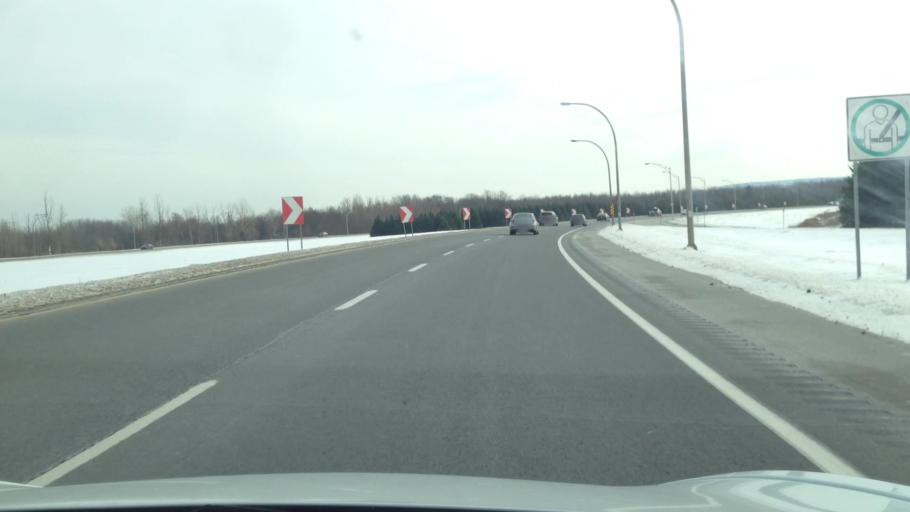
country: CA
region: Quebec
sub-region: Monteregie
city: Rigaud
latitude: 45.5371
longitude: -74.3849
